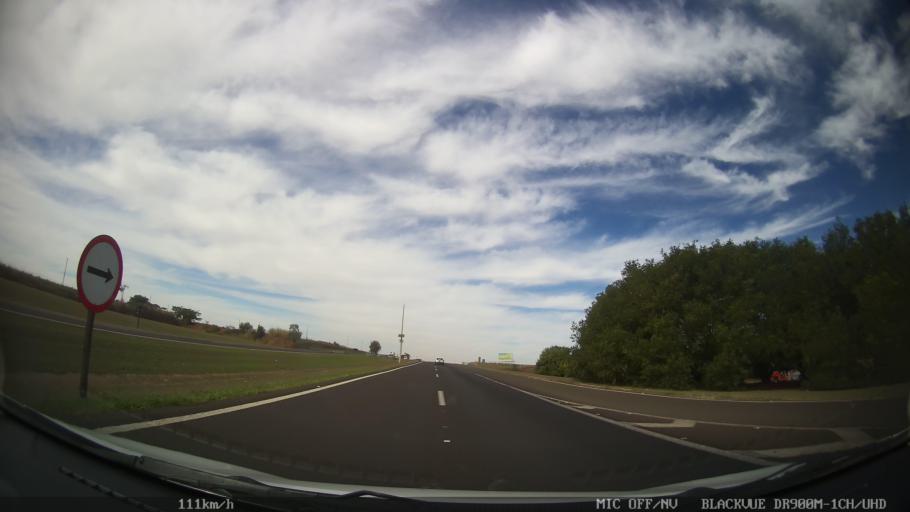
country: BR
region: Sao Paulo
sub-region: Matao
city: Matao
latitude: -21.5578
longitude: -48.4794
